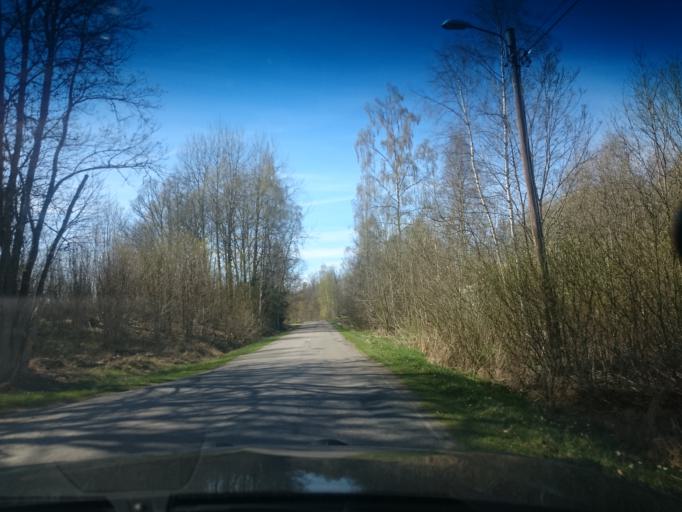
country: SE
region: Kronoberg
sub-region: Uppvidinge Kommun
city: Aseda
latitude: 57.3715
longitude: 15.3749
